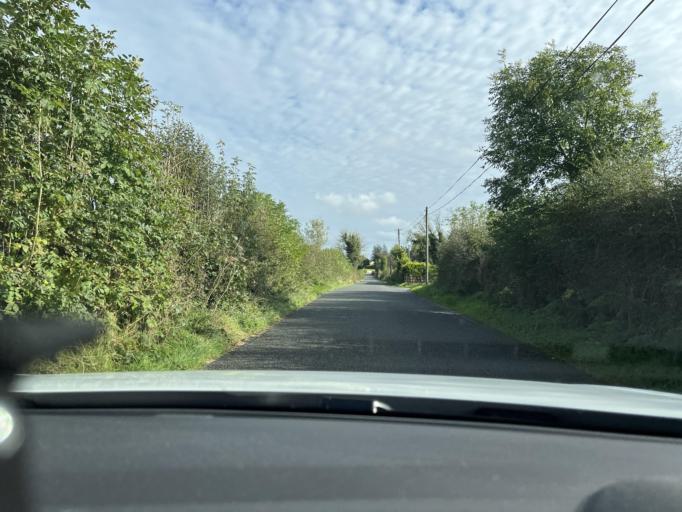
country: IE
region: Connaught
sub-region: Sligo
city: Ballymote
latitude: 54.0800
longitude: -8.4176
